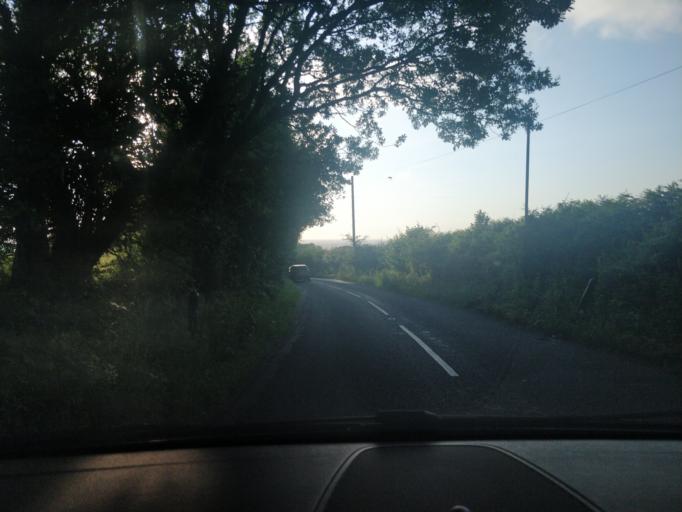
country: GB
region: England
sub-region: Lancashire
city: Skelmersdale
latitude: 53.5650
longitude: -2.7577
